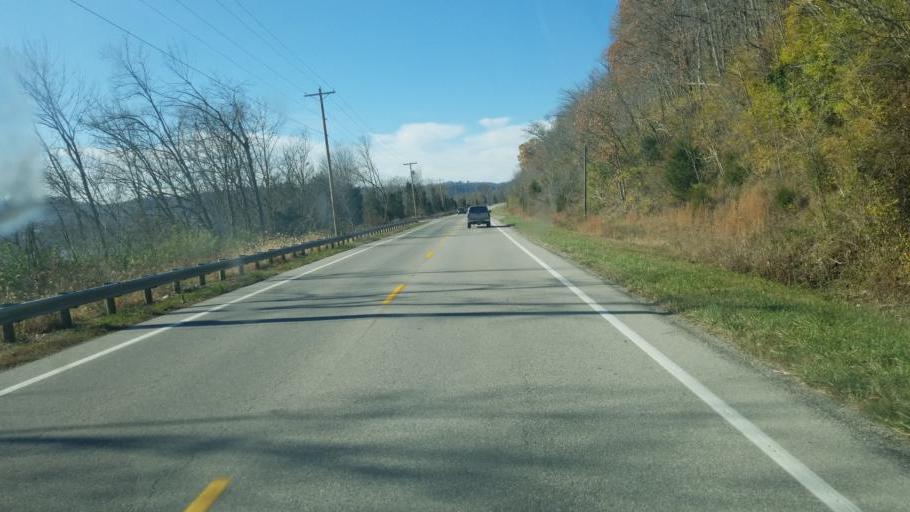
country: US
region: Kentucky
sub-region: Mason County
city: Maysville
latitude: 38.6491
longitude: -83.7340
